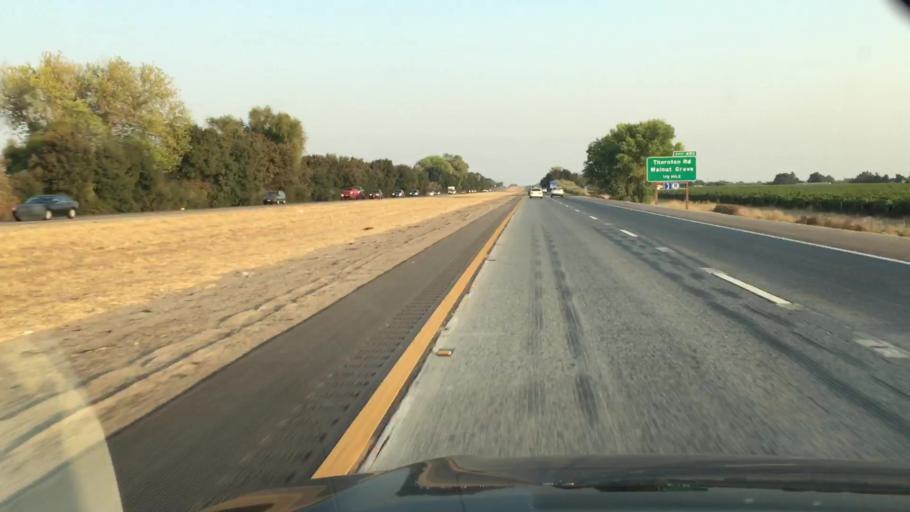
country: US
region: California
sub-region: San Joaquin County
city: Thornton
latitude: 38.2364
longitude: -121.4383
